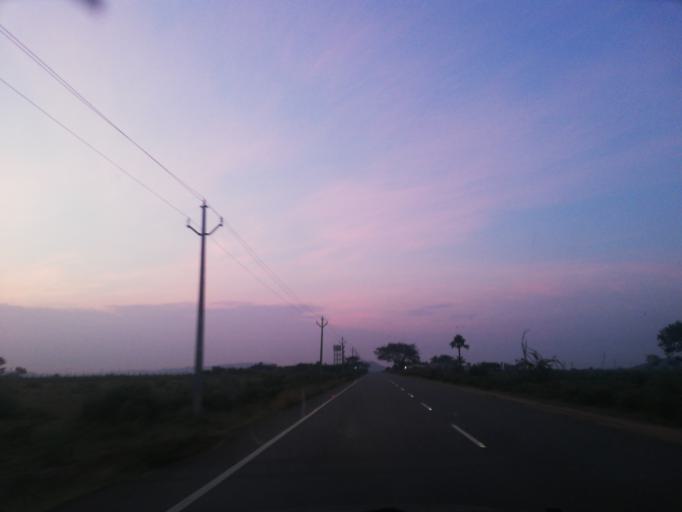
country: IN
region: Andhra Pradesh
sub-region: Guntur
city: Macherla
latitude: 16.6914
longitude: 79.2489
